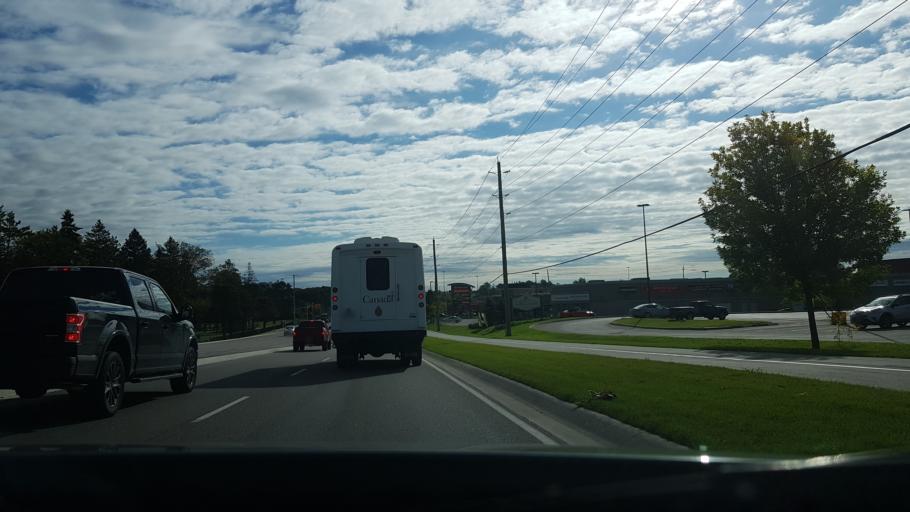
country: CA
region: Ontario
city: Orillia
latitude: 44.6118
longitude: -79.4541
